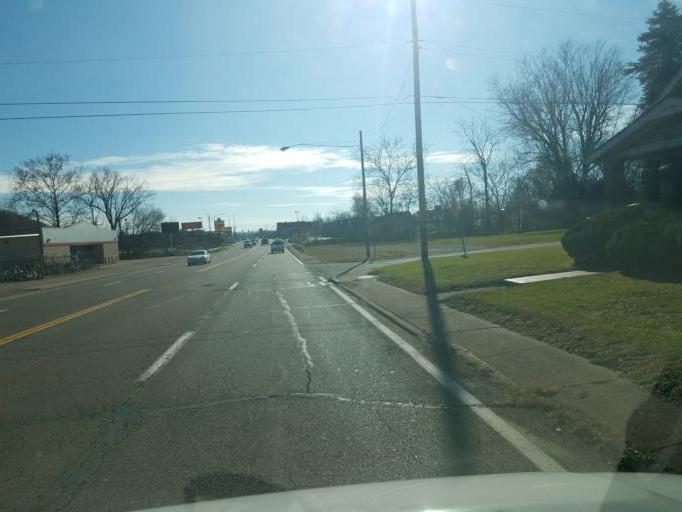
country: US
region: Ohio
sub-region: Scioto County
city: Lucasville
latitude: 38.8826
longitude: -82.9966
